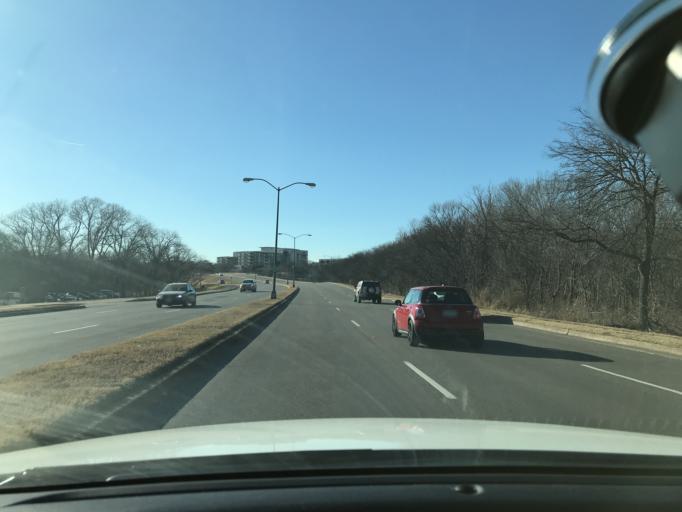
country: US
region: Texas
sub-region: Dallas County
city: Highland Park
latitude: 32.8529
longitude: -96.7245
